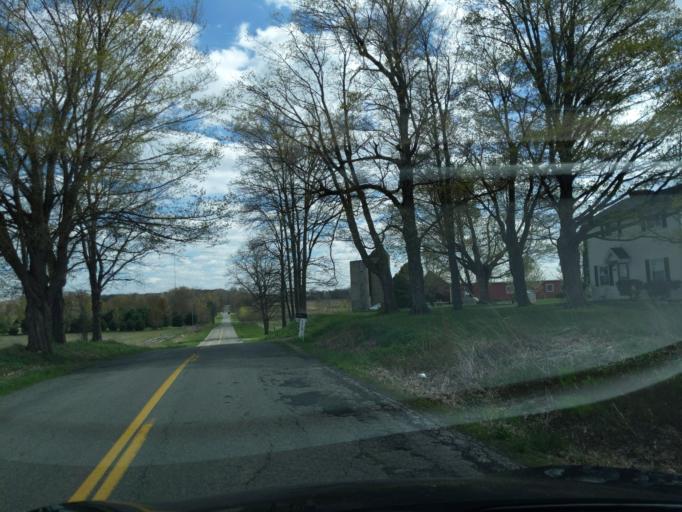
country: US
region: Michigan
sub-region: Ingham County
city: Leslie
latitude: 42.4411
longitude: -84.5263
